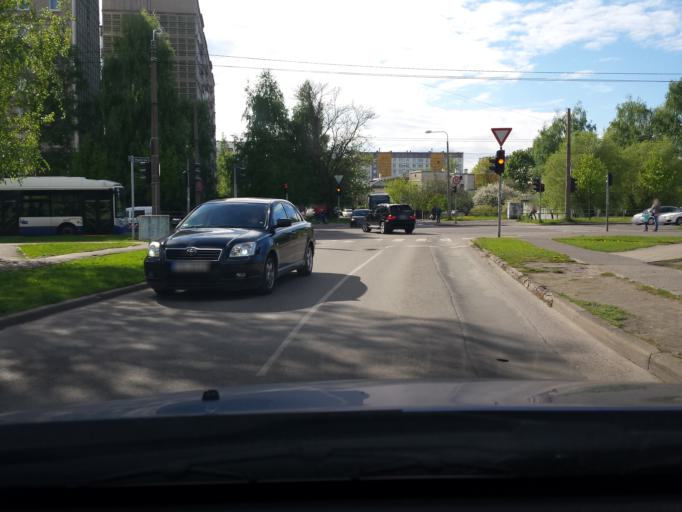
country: LV
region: Riga
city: Riga
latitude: 56.9533
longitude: 24.1754
